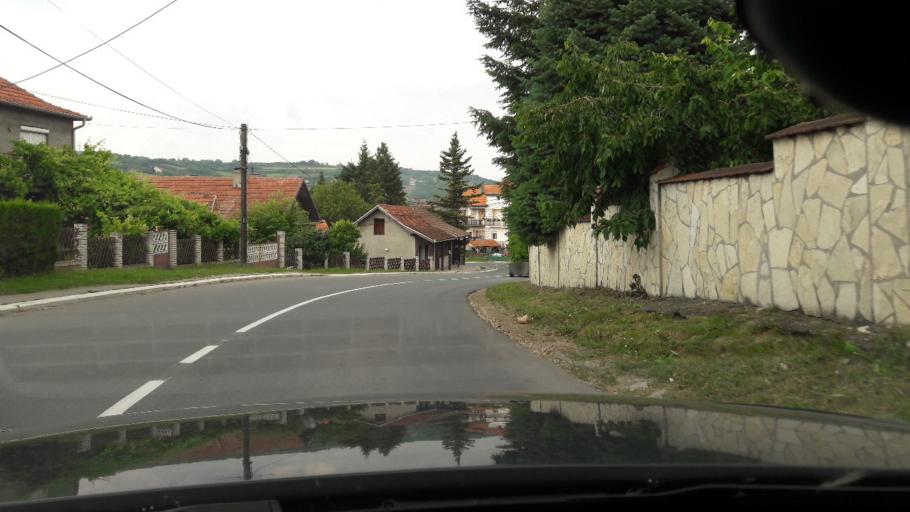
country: RS
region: Central Serbia
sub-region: Belgrade
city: Grocka
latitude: 44.6696
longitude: 20.5953
